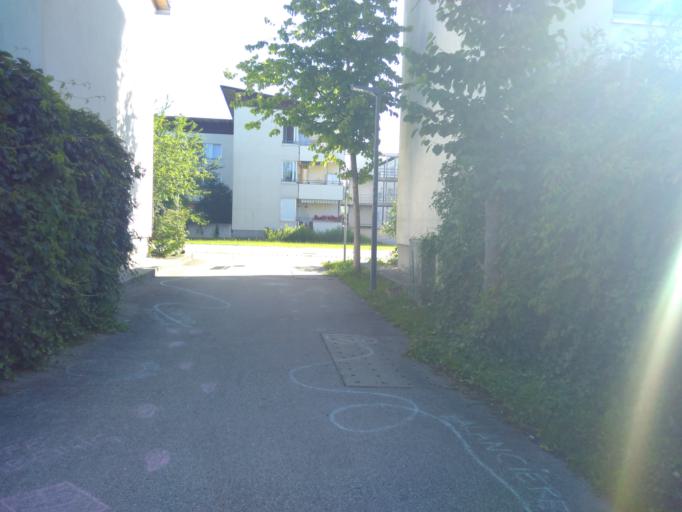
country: DE
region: Bavaria
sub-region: Upper Bavaria
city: Eichenau
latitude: 48.1777
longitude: 11.3283
